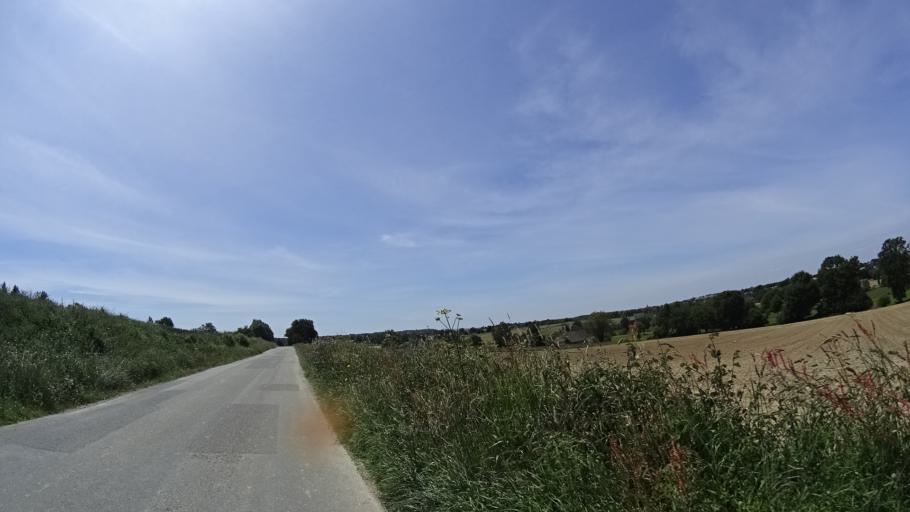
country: FR
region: Brittany
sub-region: Departement d'Ille-et-Vilaine
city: Iffendic
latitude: 48.1323
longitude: -1.9962
